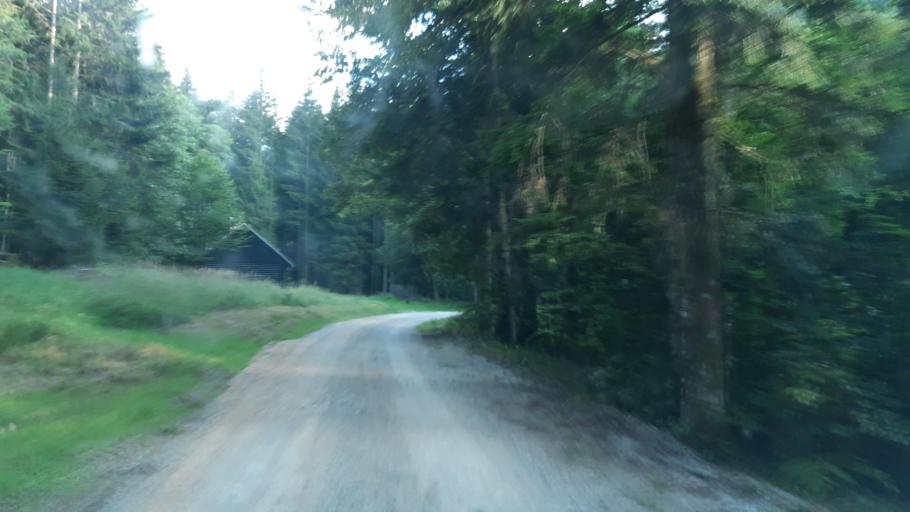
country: SI
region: Dolenjske Toplice
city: Dolenjske Toplice
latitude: 45.6888
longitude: 15.0053
